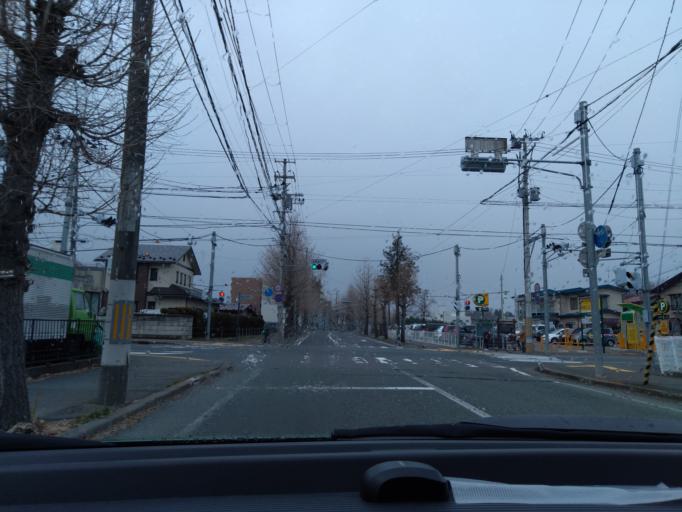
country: JP
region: Iwate
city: Morioka-shi
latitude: 39.7079
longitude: 141.1460
